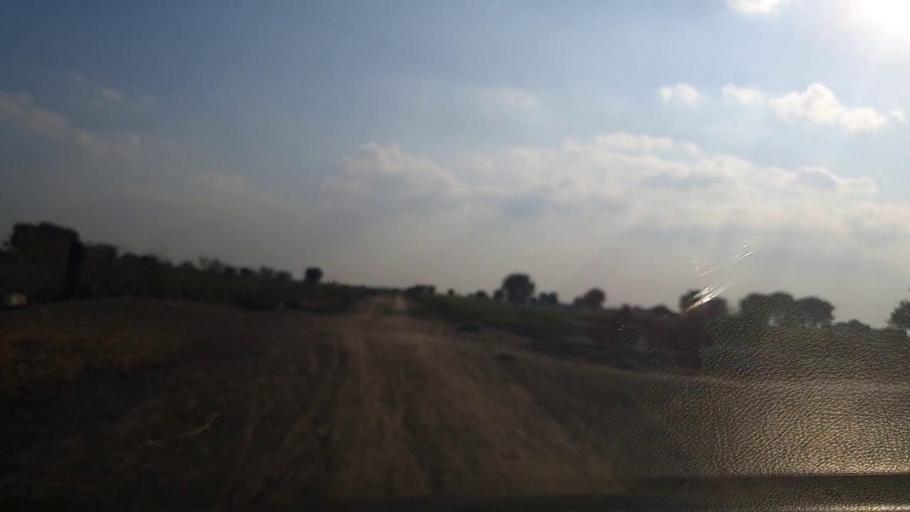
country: PK
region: Sindh
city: Jhol
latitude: 25.8317
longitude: 69.0513
